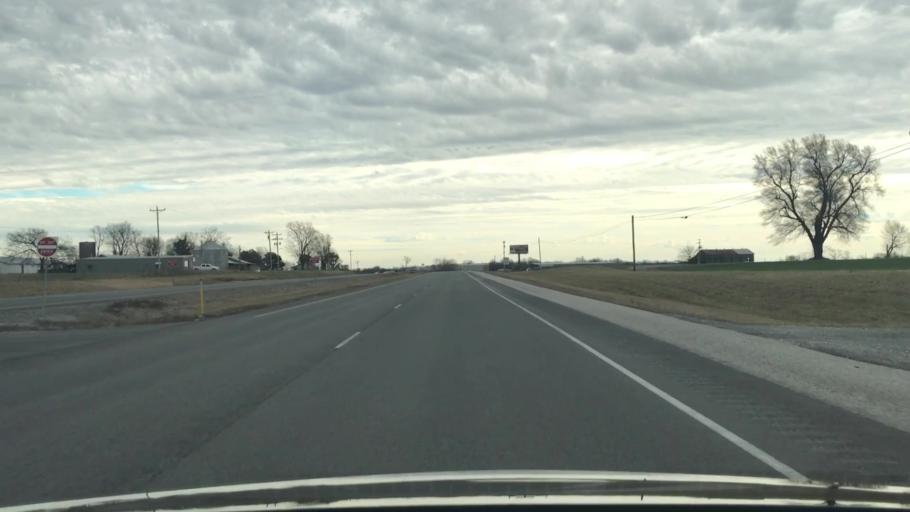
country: US
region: Kentucky
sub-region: Trigg County
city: Cadiz
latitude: 36.8858
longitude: -87.7145
